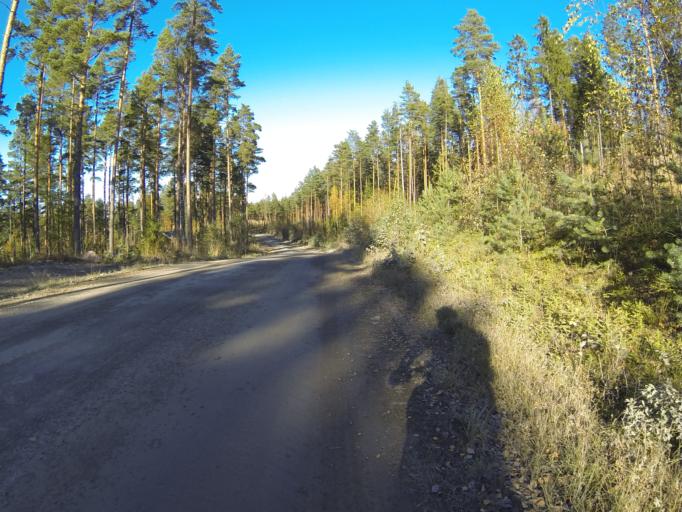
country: FI
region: Varsinais-Suomi
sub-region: Salo
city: Saerkisalo
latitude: 60.2188
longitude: 22.9903
